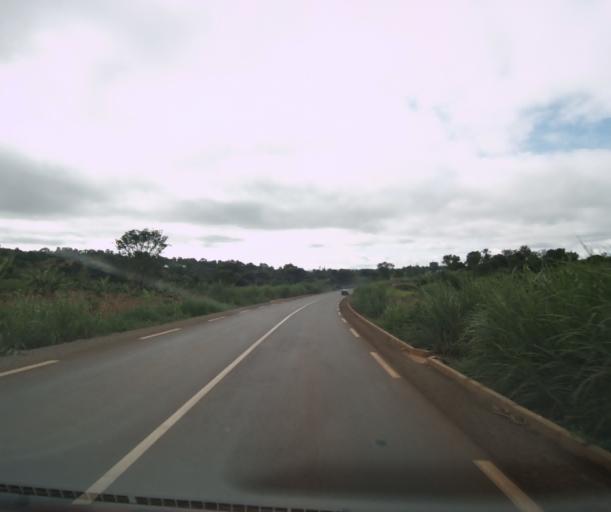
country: CM
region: West
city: Bansoa
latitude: 5.5297
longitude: 10.3359
